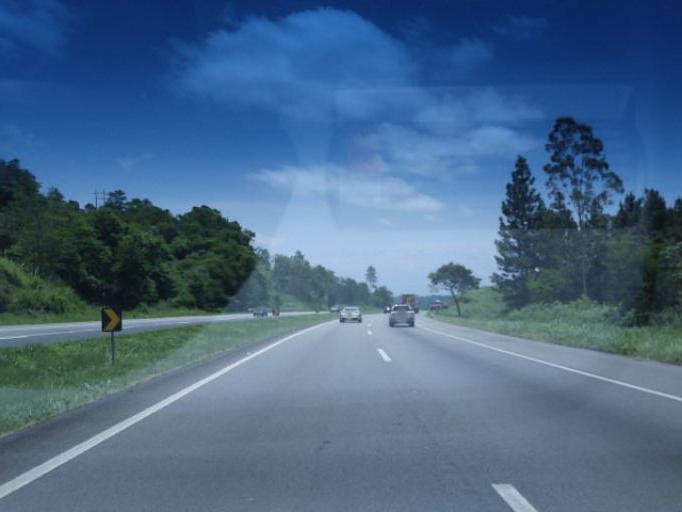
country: BR
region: Sao Paulo
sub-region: Miracatu
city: Miracatu
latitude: -24.3068
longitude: -47.4947
